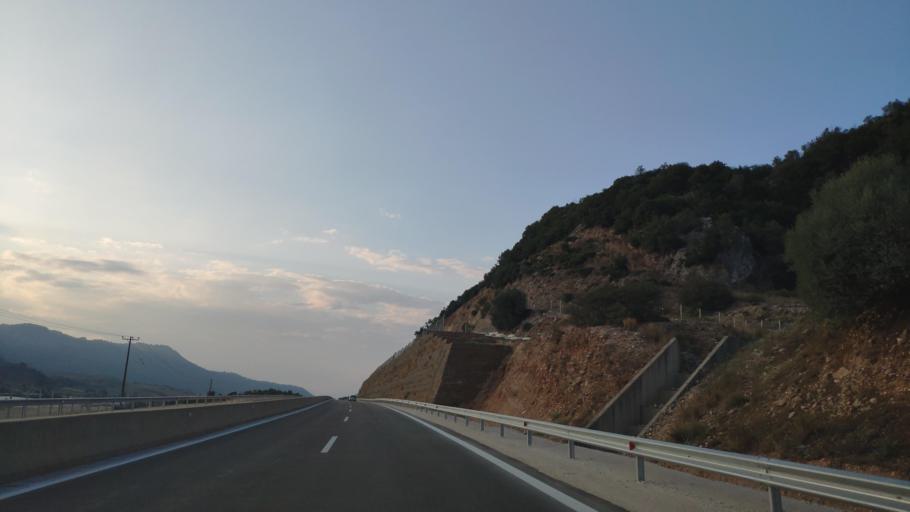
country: GR
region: West Greece
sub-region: Nomos Aitolias kai Akarnanias
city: Katouna
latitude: 38.7931
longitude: 21.1405
